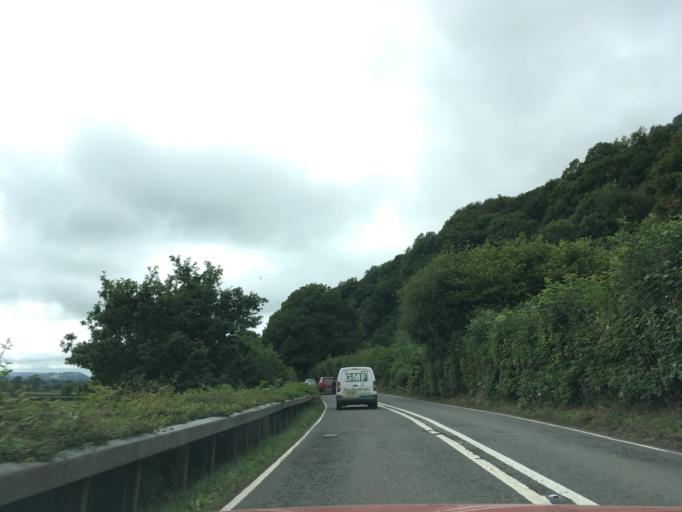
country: GB
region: Wales
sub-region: Carmarthenshire
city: Llanddarog
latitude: 51.8737
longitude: -4.2060
